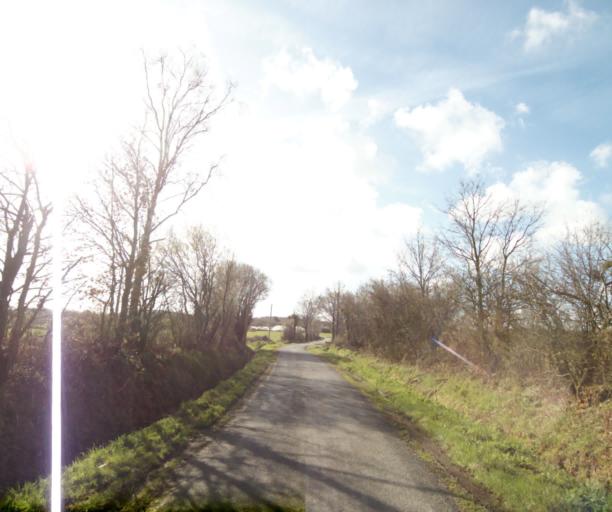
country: FR
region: Pays de la Loire
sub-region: Departement de la Loire-Atlantique
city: Bouvron
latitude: 47.4079
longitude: -1.8531
